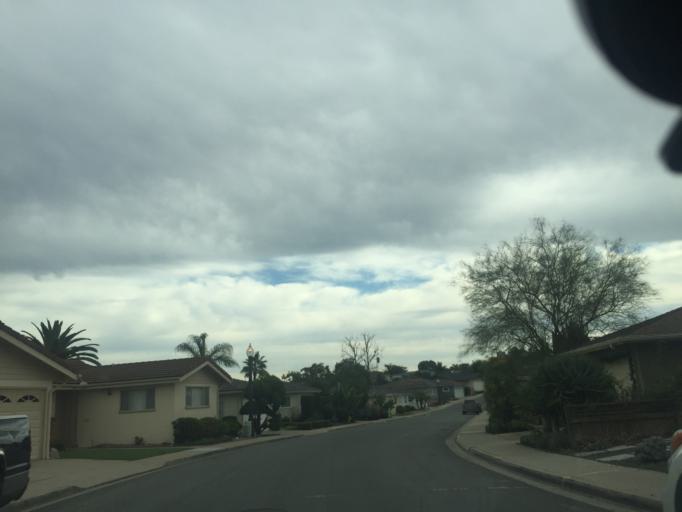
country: US
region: California
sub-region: San Diego County
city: Lemon Grove
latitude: 32.7699
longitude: -117.0945
